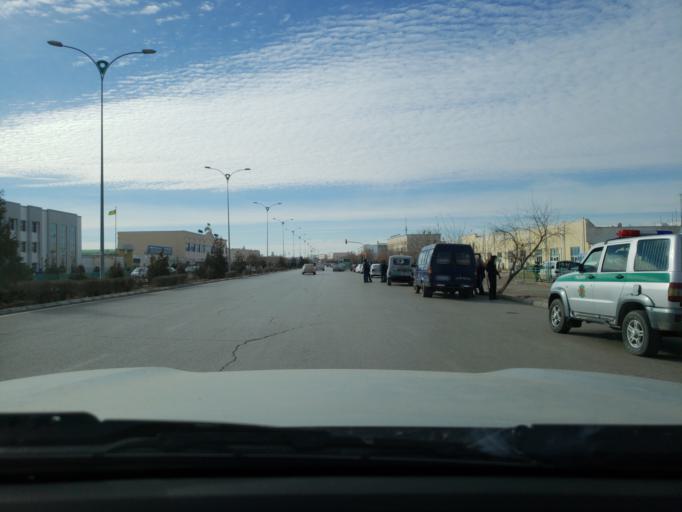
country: TM
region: Dasoguz
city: Dasoguz
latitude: 41.8490
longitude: 59.9655
